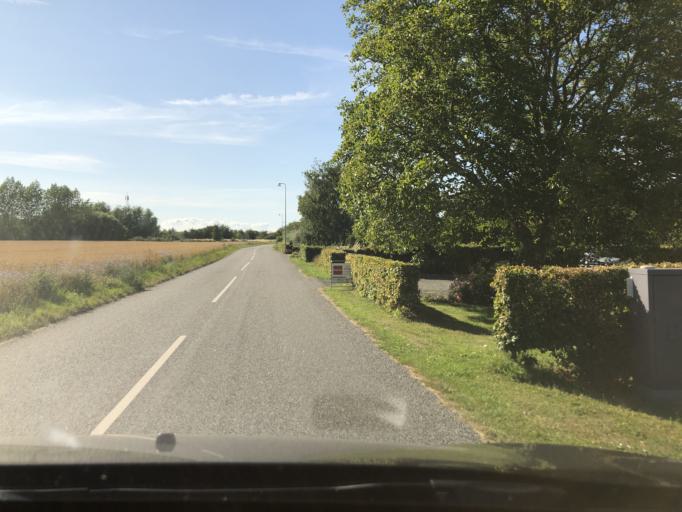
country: DK
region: South Denmark
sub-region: AEro Kommune
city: Marstal
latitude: 54.8679
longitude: 10.5001
